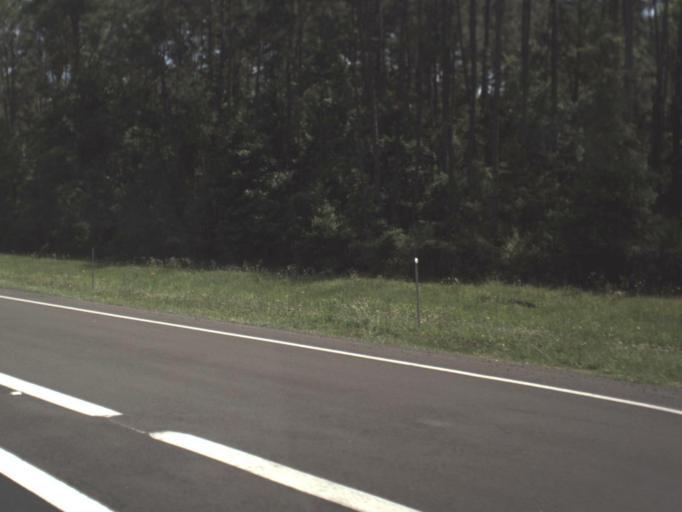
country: US
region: Florida
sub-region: Nassau County
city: Yulee
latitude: 30.5225
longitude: -81.6355
